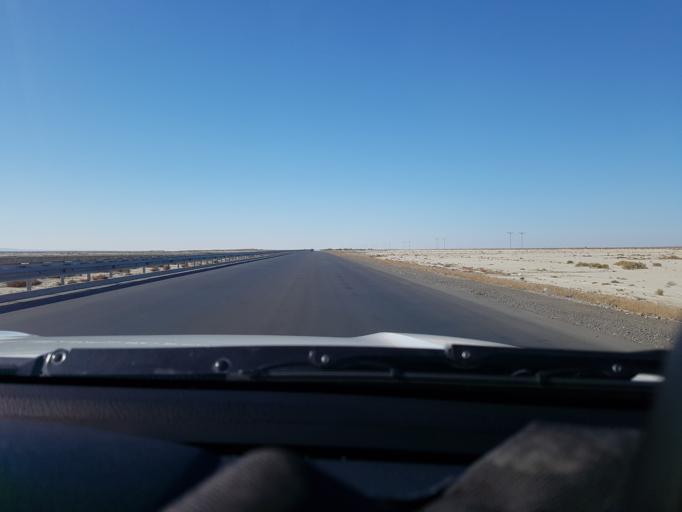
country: TM
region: Balkan
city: Gazanjyk
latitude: 39.2508
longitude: 55.0995
